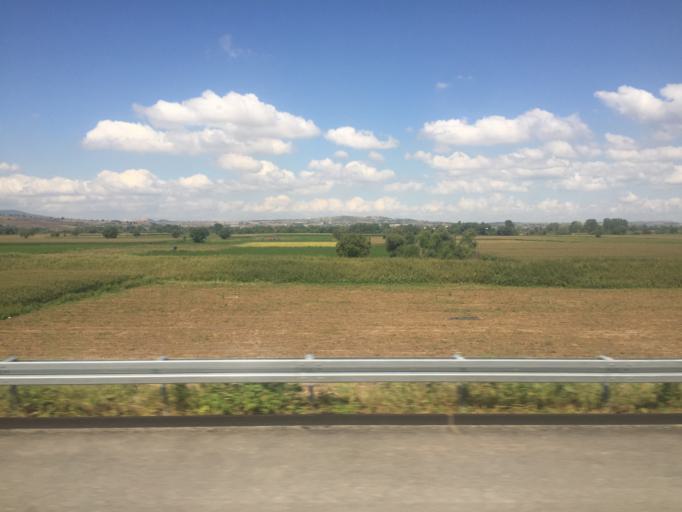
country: TR
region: Balikesir
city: Gobel
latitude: 40.0094
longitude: 28.1970
